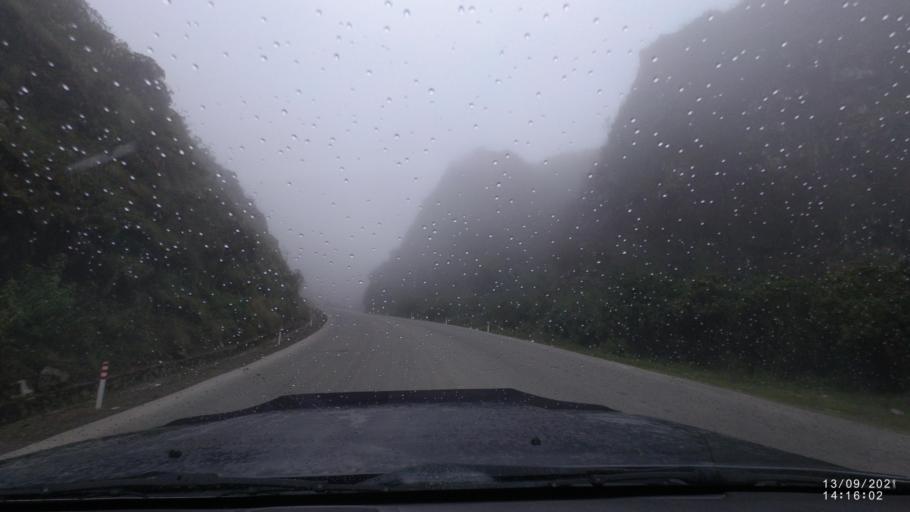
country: BO
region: Cochabamba
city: Colomi
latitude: -17.2127
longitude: -65.8894
